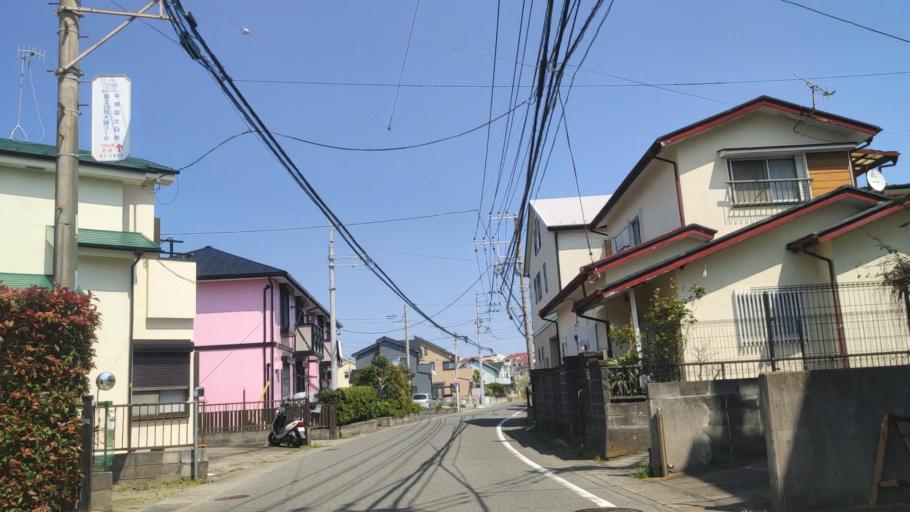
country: JP
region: Kanagawa
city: Hiratsuka
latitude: 35.3157
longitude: 139.3256
